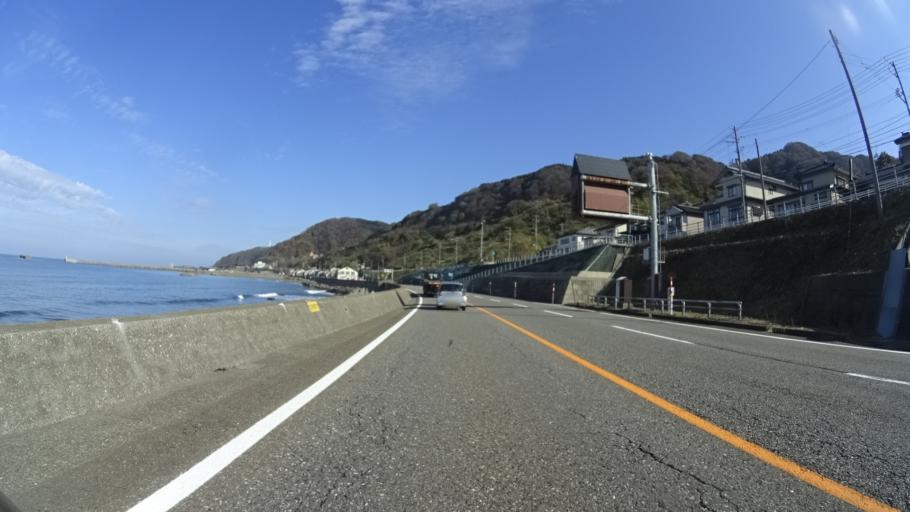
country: JP
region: Niigata
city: Joetsu
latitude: 37.1265
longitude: 138.0466
